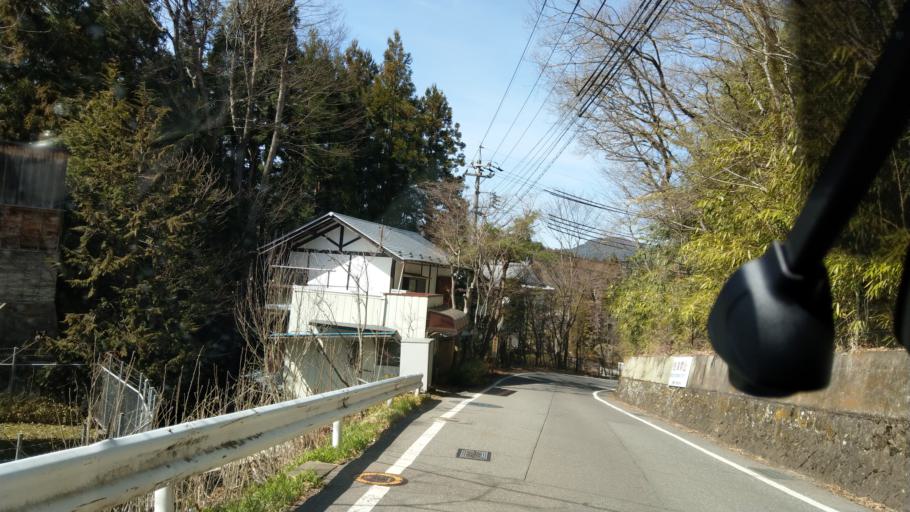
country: JP
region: Nagano
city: Kamimaruko
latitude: 36.3501
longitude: 138.1603
